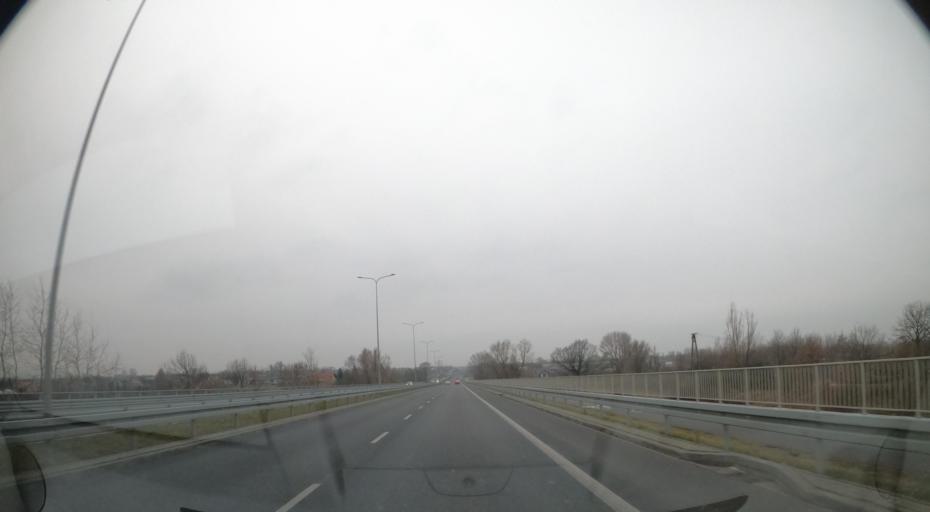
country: PL
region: Masovian Voivodeship
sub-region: Radom
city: Radom
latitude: 51.4062
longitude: 21.2020
